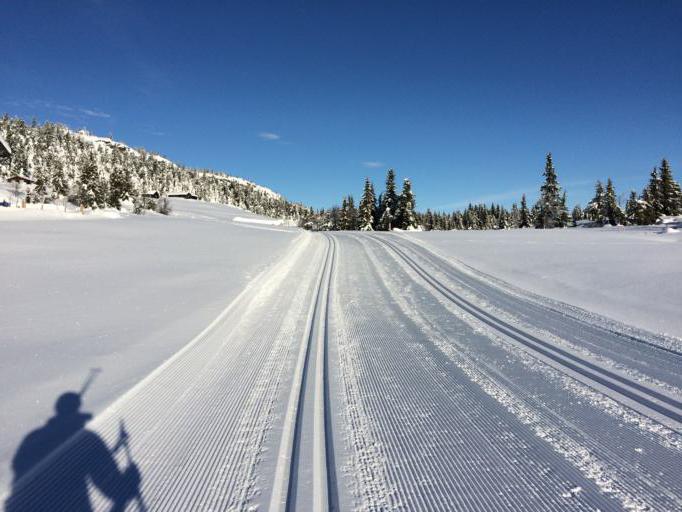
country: NO
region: Oppland
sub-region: Gausdal
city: Segalstad bru
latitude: 61.3161
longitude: 10.0617
